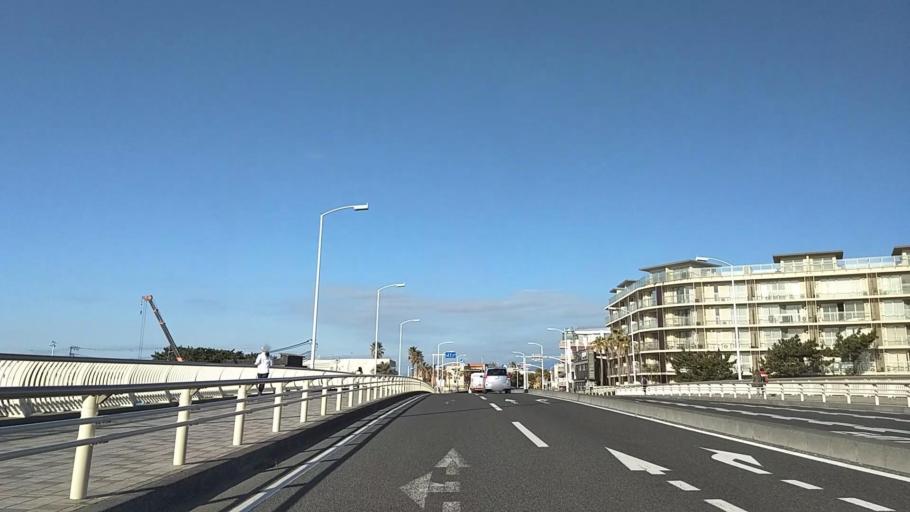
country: JP
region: Kanagawa
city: Fujisawa
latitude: 35.3075
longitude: 139.4840
